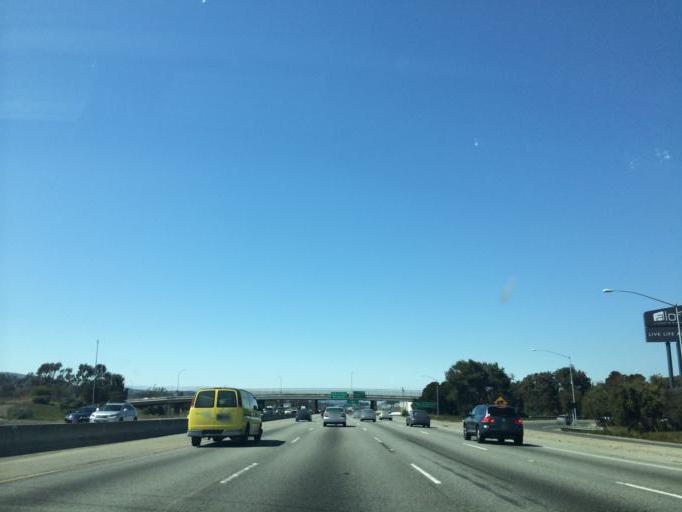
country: US
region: California
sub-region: San Mateo County
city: Millbrae
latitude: 37.6011
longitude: -122.3781
